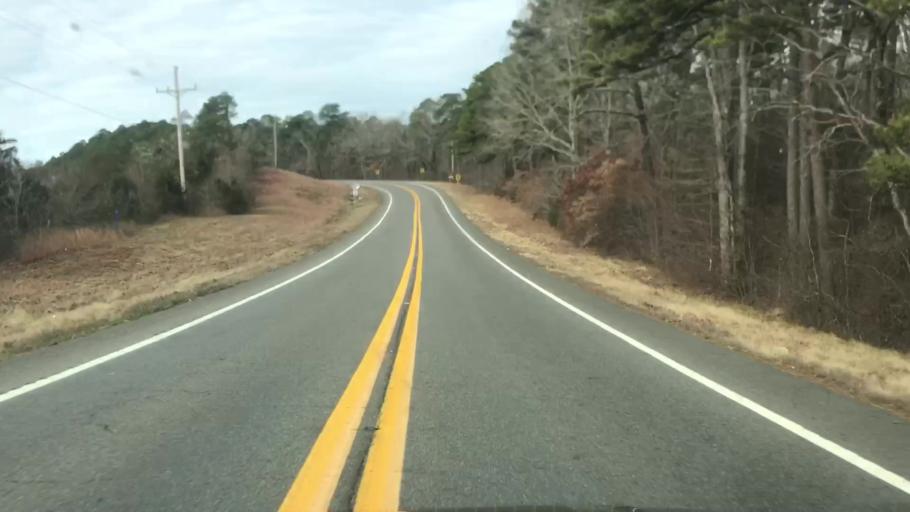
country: US
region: Arkansas
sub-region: Montgomery County
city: Mount Ida
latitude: 34.6198
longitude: -93.7080
